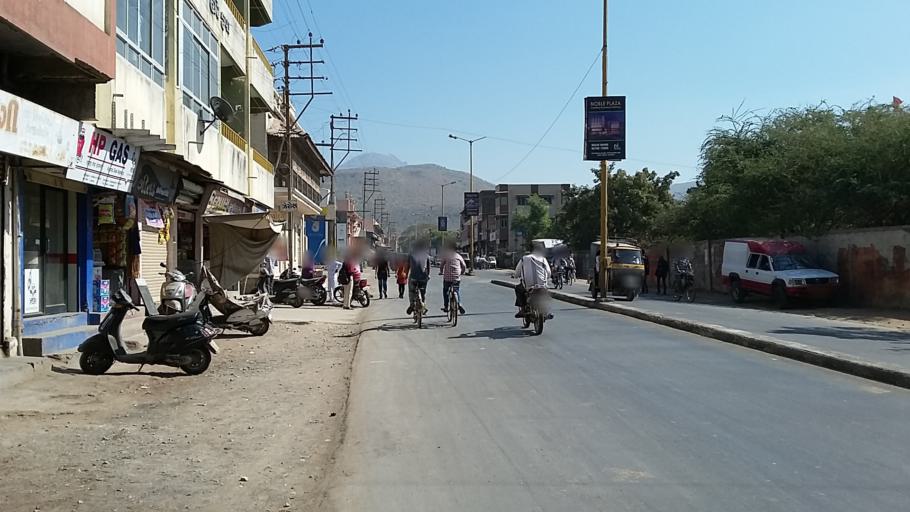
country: IN
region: Gujarat
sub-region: Junagadh
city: Junagadh
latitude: 21.5112
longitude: 70.4606
